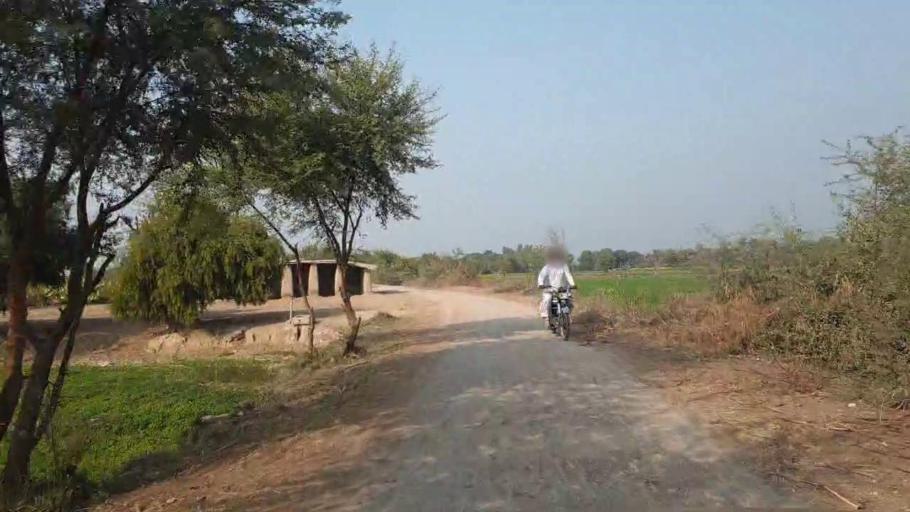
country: PK
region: Sindh
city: Bhit Shah
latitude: 25.8888
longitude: 68.4753
